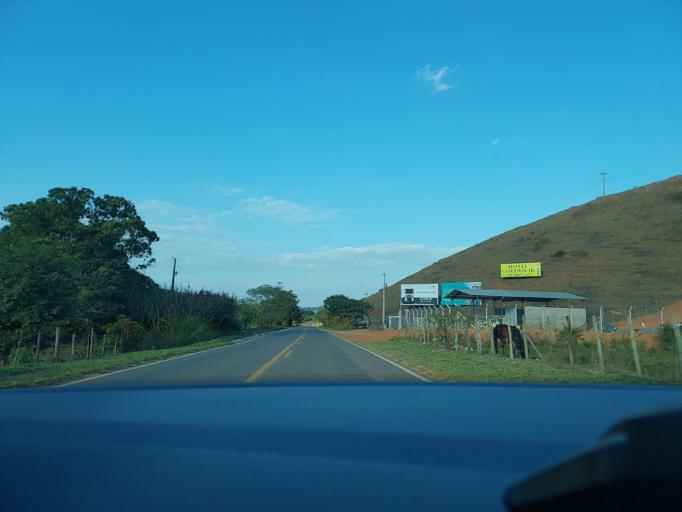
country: BR
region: Minas Gerais
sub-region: Muriae
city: Muriae
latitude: -21.1186
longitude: -42.4225
